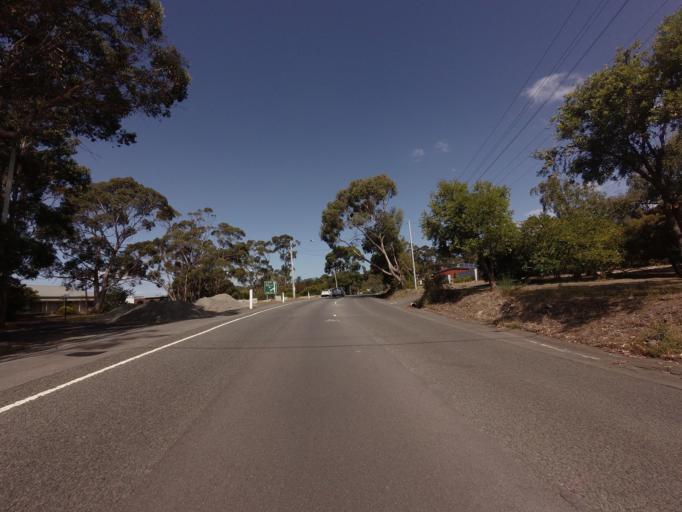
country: AU
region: Tasmania
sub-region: Hobart
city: Dynnyrne
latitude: -42.9190
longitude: 147.3214
